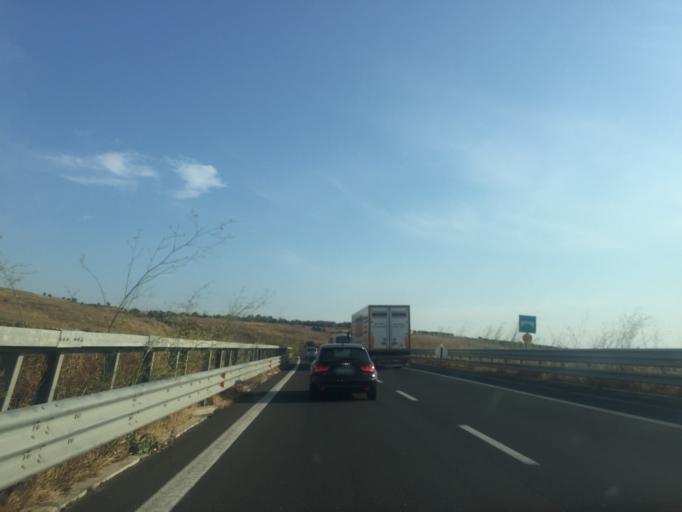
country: IT
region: Sicily
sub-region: Provincia di Siracusa
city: Lentini
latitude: 37.3566
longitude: 15.0474
